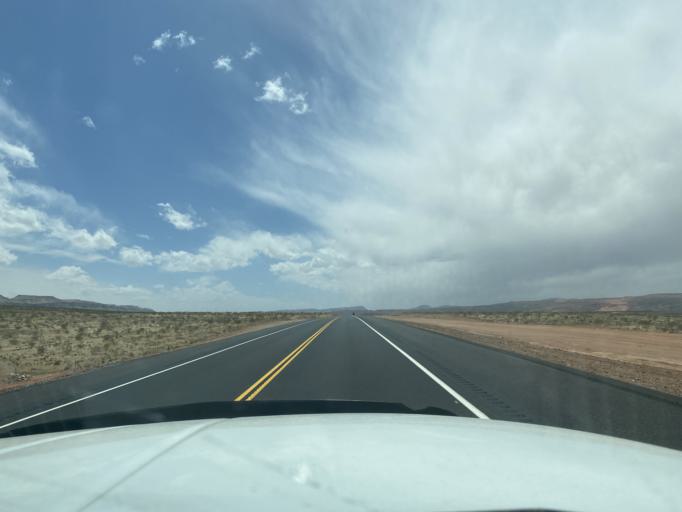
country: US
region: Utah
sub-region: Washington County
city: Hurricane
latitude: 37.1542
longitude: -113.3458
